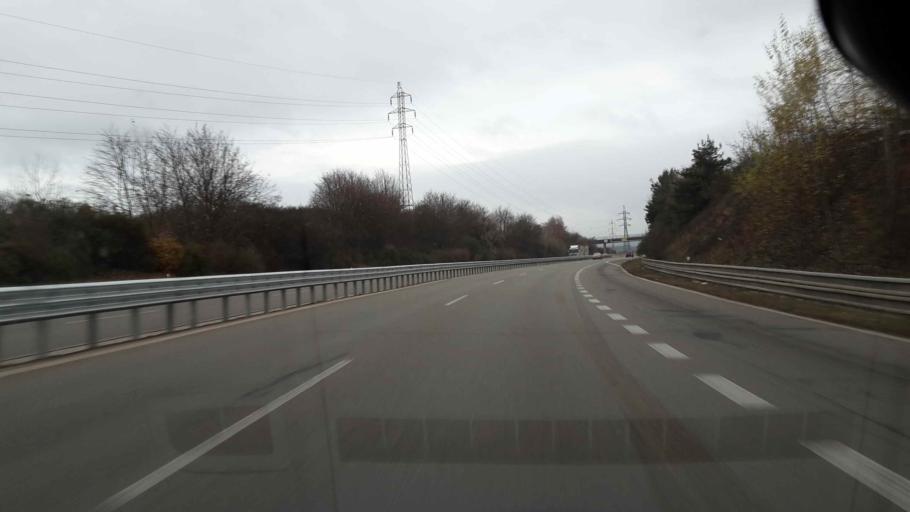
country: CZ
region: South Moravian
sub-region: Mesto Brno
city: Mokra Hora
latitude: 49.2628
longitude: 16.5750
